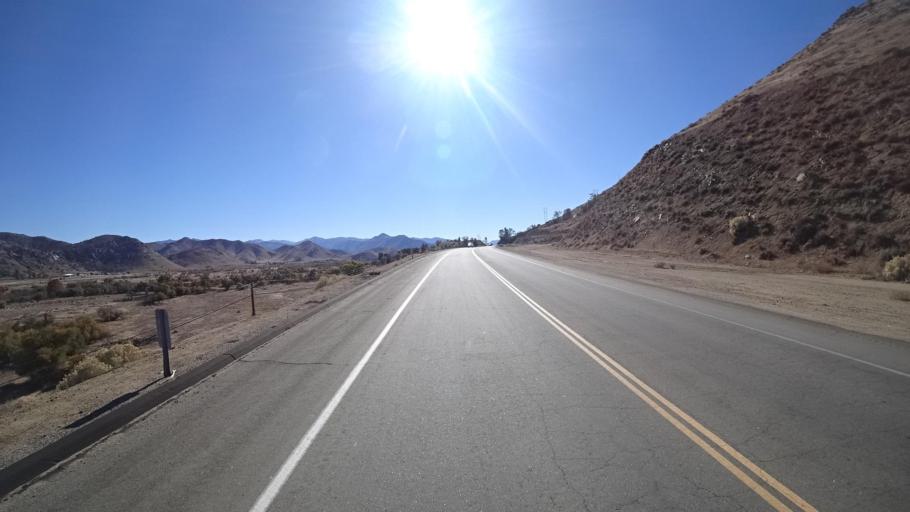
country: US
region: California
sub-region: Kern County
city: Kernville
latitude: 35.7336
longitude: -118.4279
